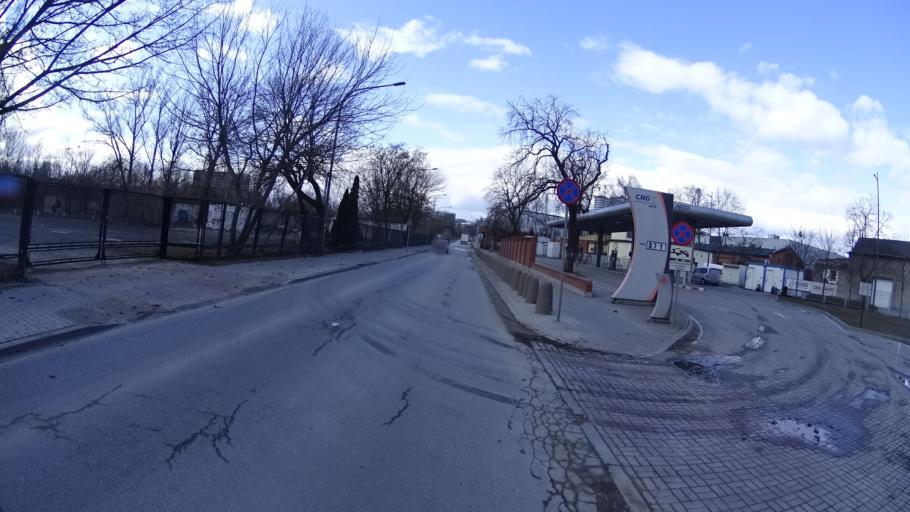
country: PL
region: Masovian Voivodeship
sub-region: Warszawa
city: Ochota
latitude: 52.2241
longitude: 20.9647
